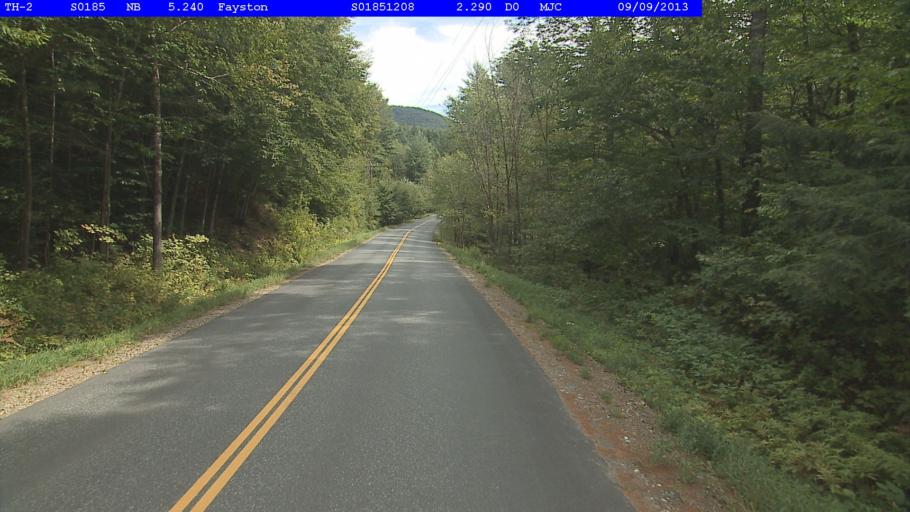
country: US
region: Vermont
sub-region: Washington County
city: Waterbury
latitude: 44.1837
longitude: -72.8773
